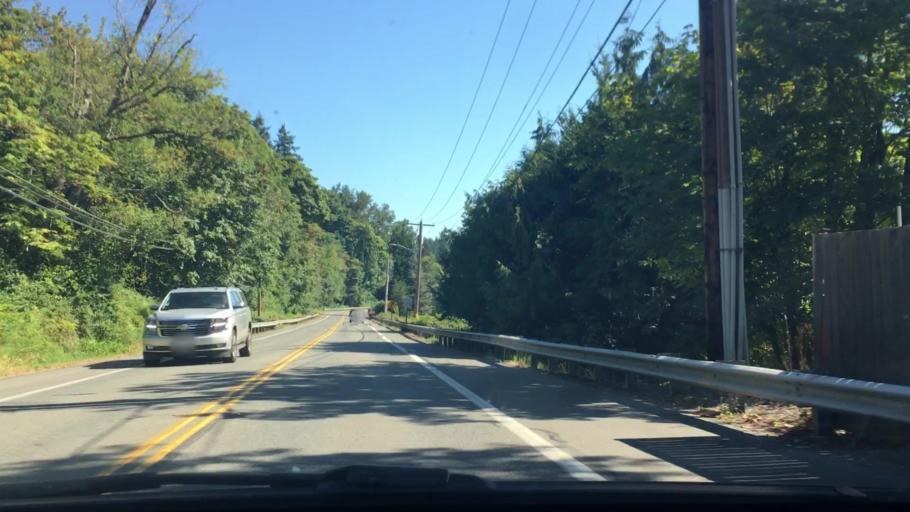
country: US
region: Washington
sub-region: King County
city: Sammamish
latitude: 47.6200
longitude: -122.0684
